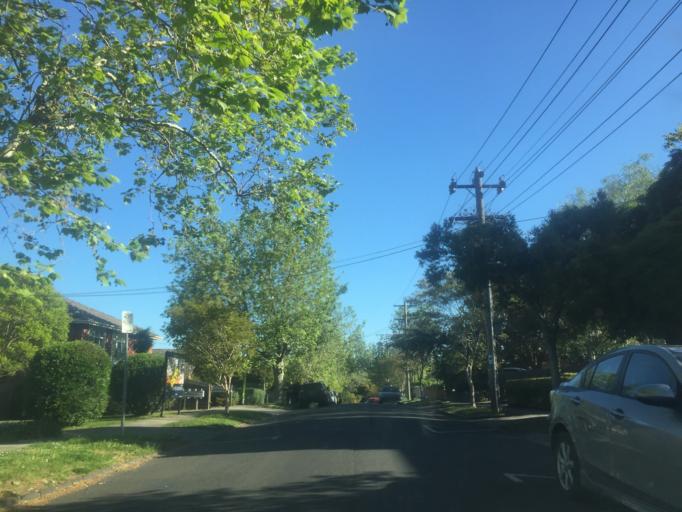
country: AU
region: Victoria
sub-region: Boroondara
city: Canterbury
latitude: -37.8151
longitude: 145.0841
